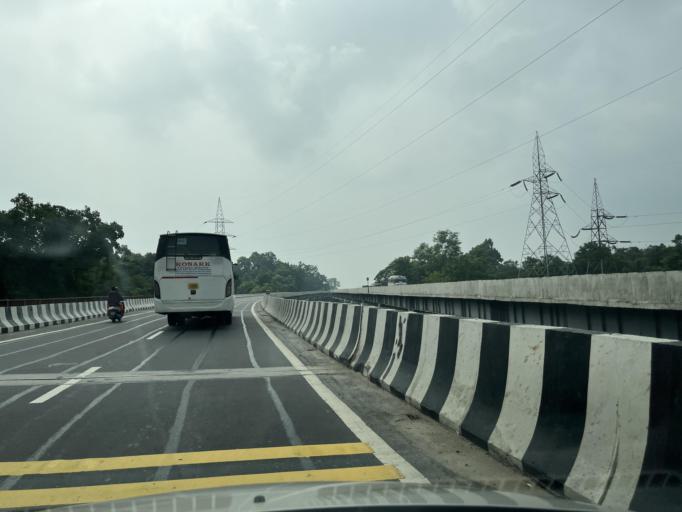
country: IN
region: Uttarakhand
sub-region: Dehradun
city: Raiwala
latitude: 30.0699
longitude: 78.2061
